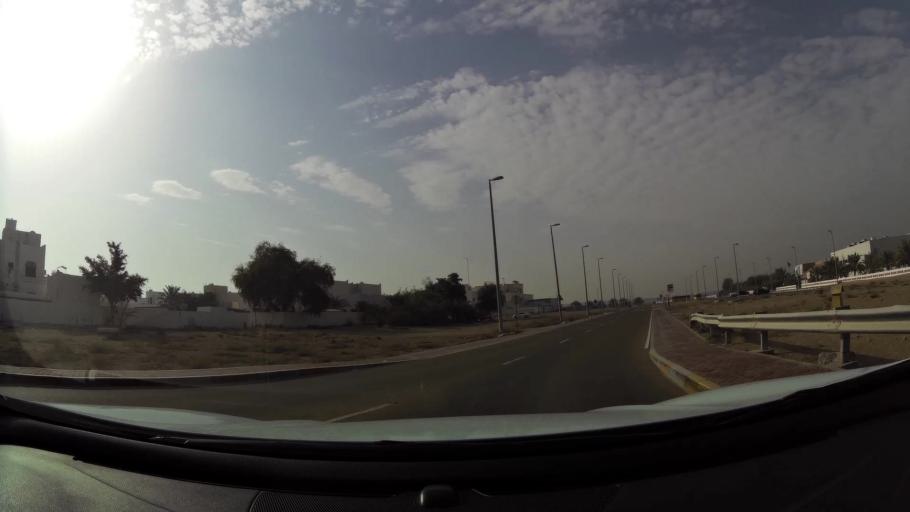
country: AE
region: Abu Dhabi
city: Abu Dhabi
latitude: 24.2449
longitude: 54.7109
